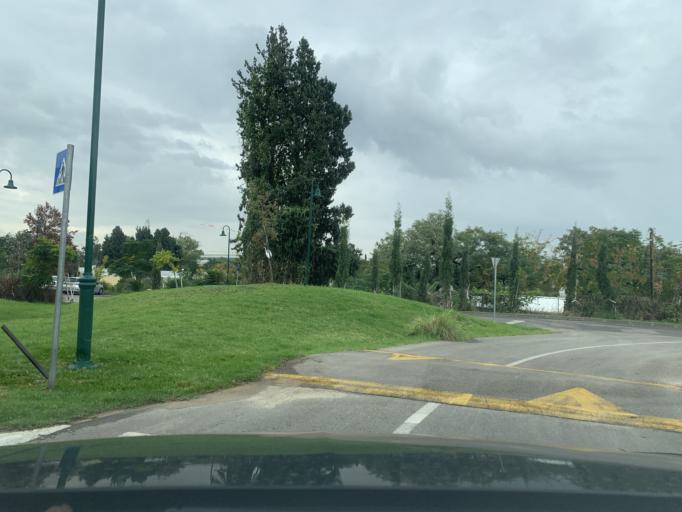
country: PS
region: West Bank
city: Qalqilyah
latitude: 32.2113
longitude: 34.9821
